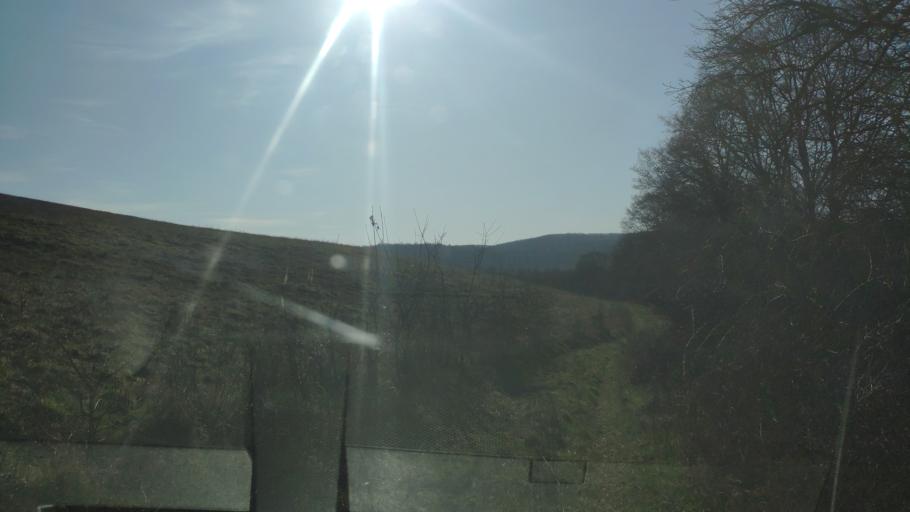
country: SK
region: Banskobystricky
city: Revuca
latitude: 48.5422
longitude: 20.2474
